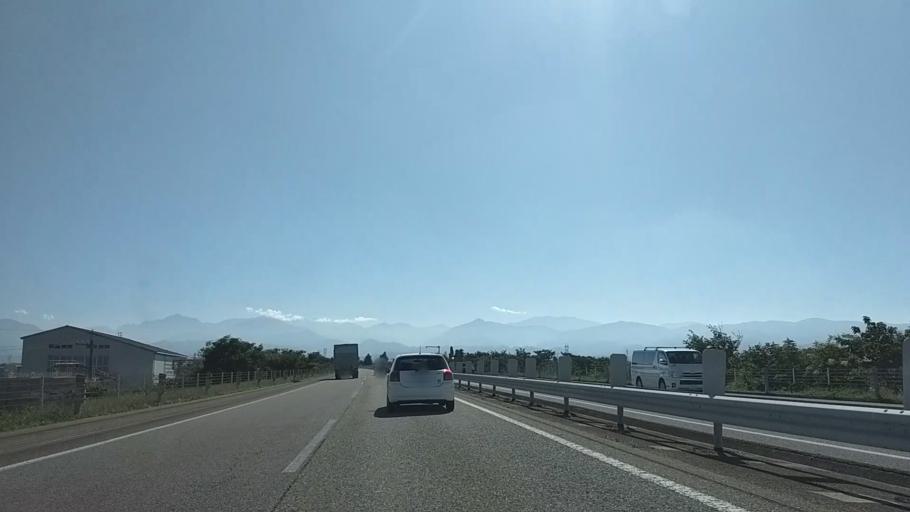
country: JP
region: Toyama
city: Toyama-shi
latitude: 36.6480
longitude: 137.2212
